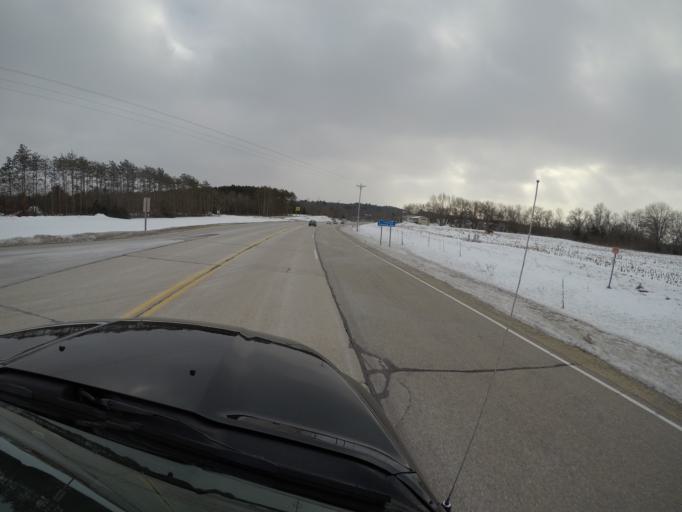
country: US
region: Wisconsin
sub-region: Trempealeau County
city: Galesville
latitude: 44.0661
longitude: -91.2919
